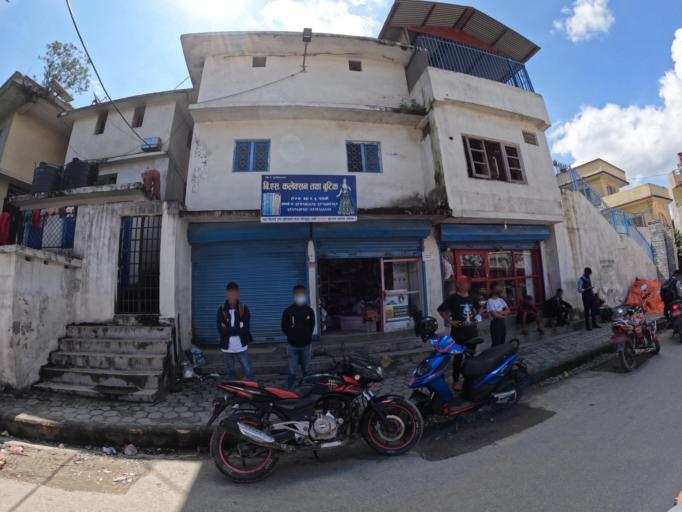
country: NP
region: Central Region
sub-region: Bagmati Zone
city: Kathmandu
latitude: 27.7426
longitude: 85.3295
